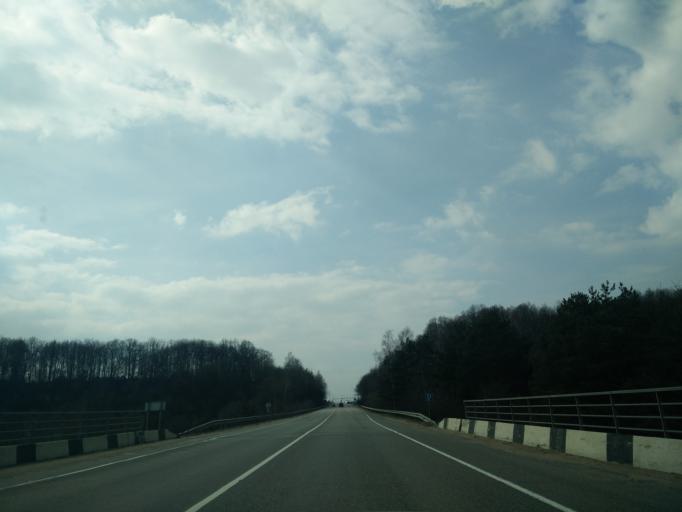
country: LT
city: Grigiskes
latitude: 54.6262
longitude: 25.1215
